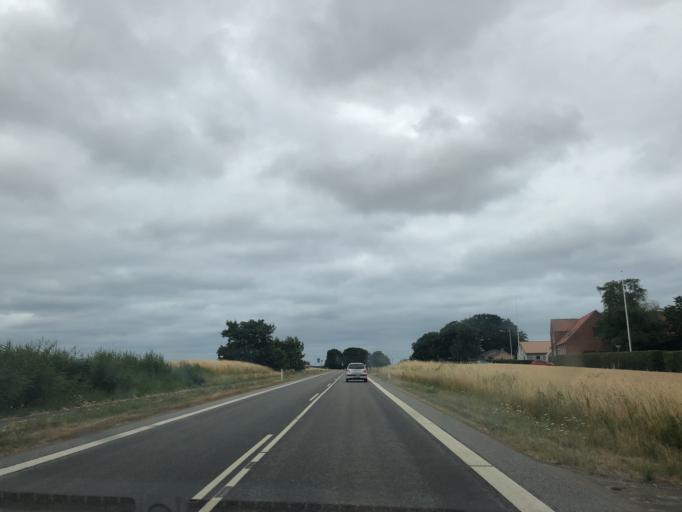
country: DK
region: Zealand
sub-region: Slagelse Kommune
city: Skaelskor
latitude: 55.2226
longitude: 11.3053
